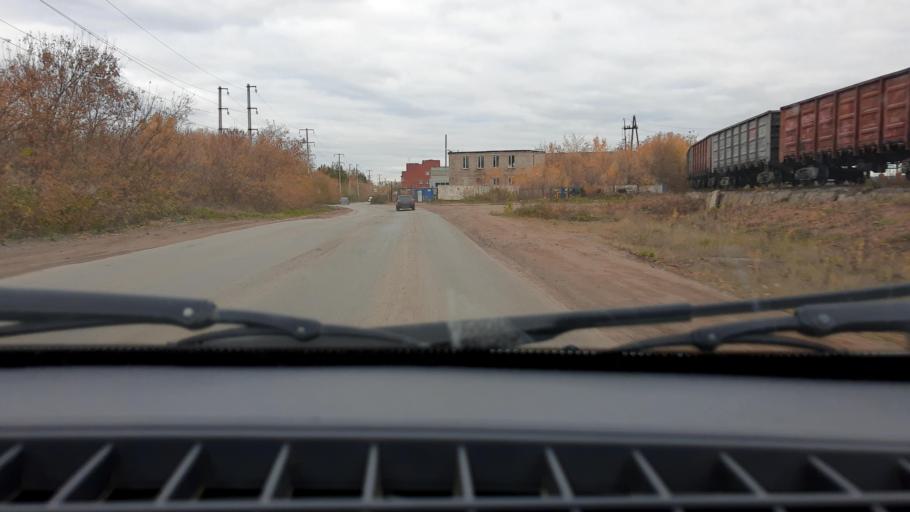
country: RU
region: Bashkortostan
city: Ufa
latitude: 54.5727
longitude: 55.9237
